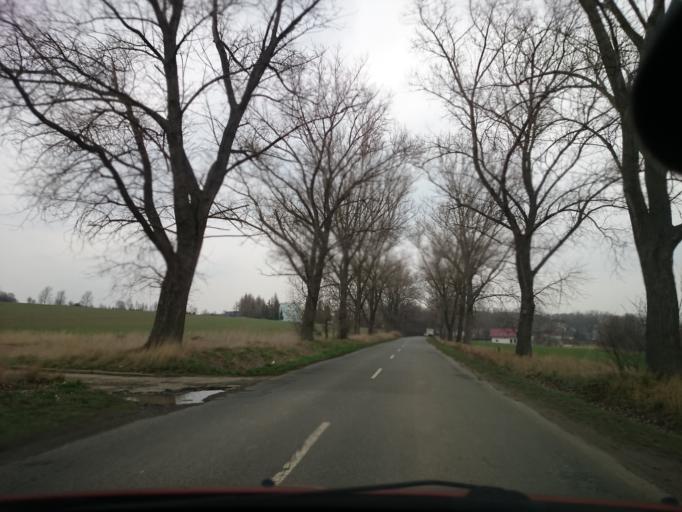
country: PL
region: Lower Silesian Voivodeship
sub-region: Powiat klodzki
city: Polanica-Zdroj
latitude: 50.4221
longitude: 16.5380
